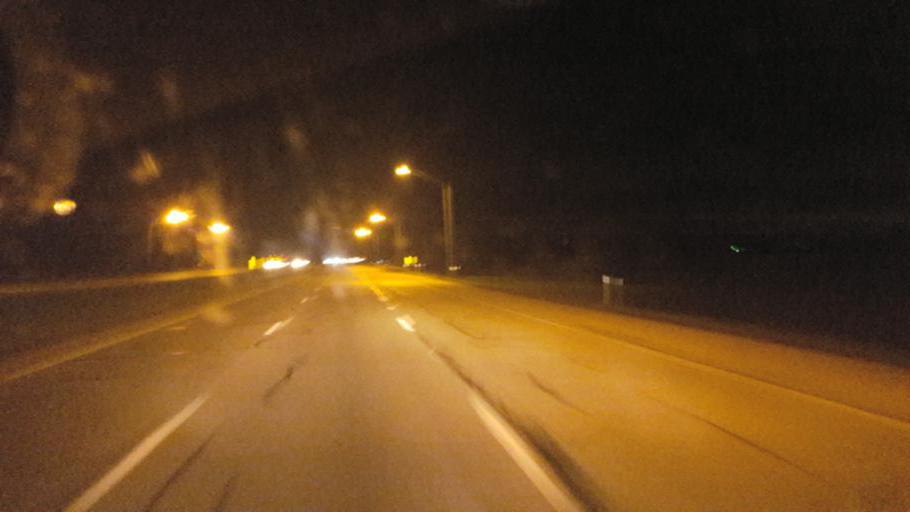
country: US
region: Indiana
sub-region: Wayne County
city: Cambridge City
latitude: 39.8522
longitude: -85.2679
